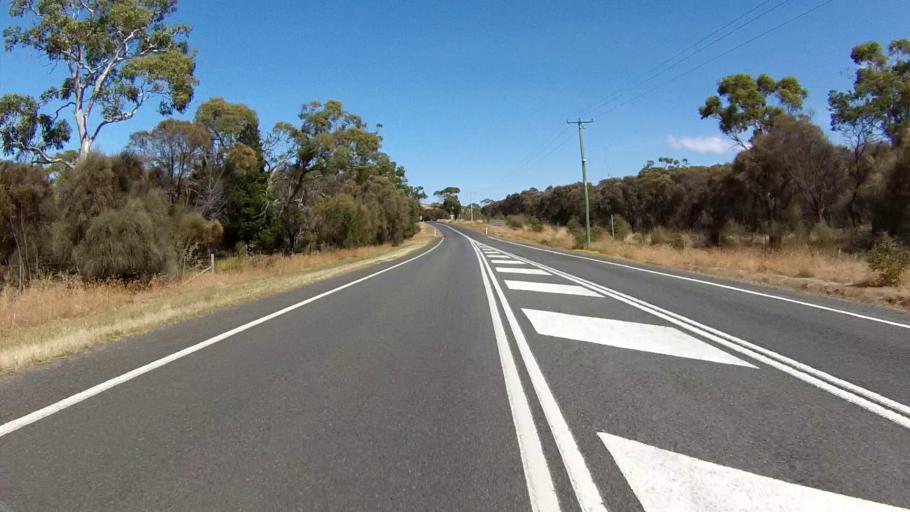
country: AU
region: Tasmania
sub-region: Sorell
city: Sorell
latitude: -42.1434
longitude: 148.0685
